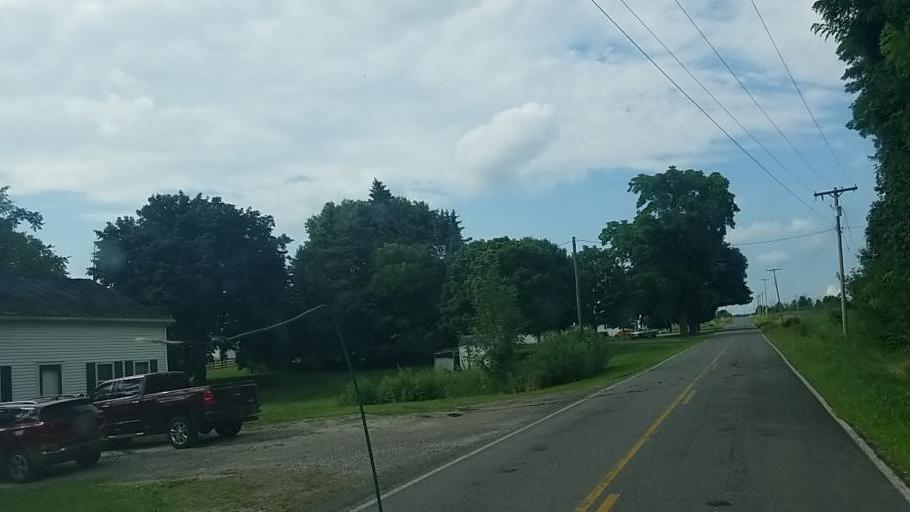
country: US
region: Ohio
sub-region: Medina County
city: Westfield Center
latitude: 41.0062
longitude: -81.9411
